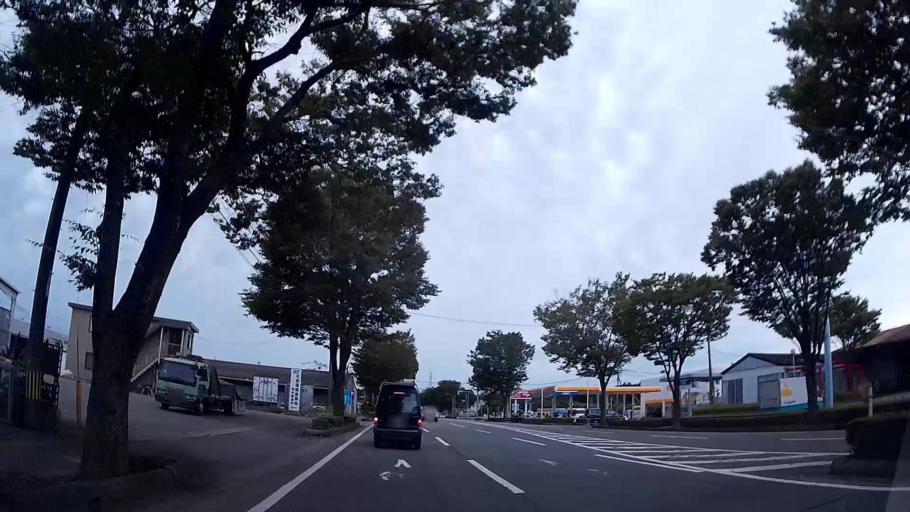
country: JP
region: Kumamoto
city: Ozu
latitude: 32.8973
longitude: 130.8535
